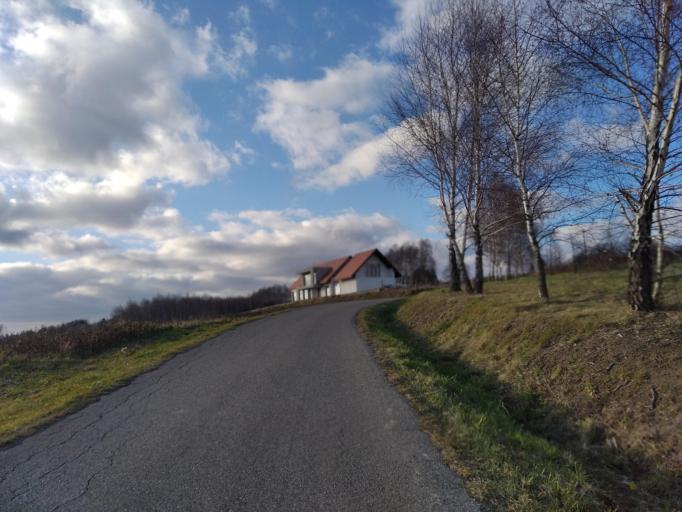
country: PL
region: Subcarpathian Voivodeship
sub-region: Powiat strzyzowski
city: Babica
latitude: 49.9434
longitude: 21.8874
